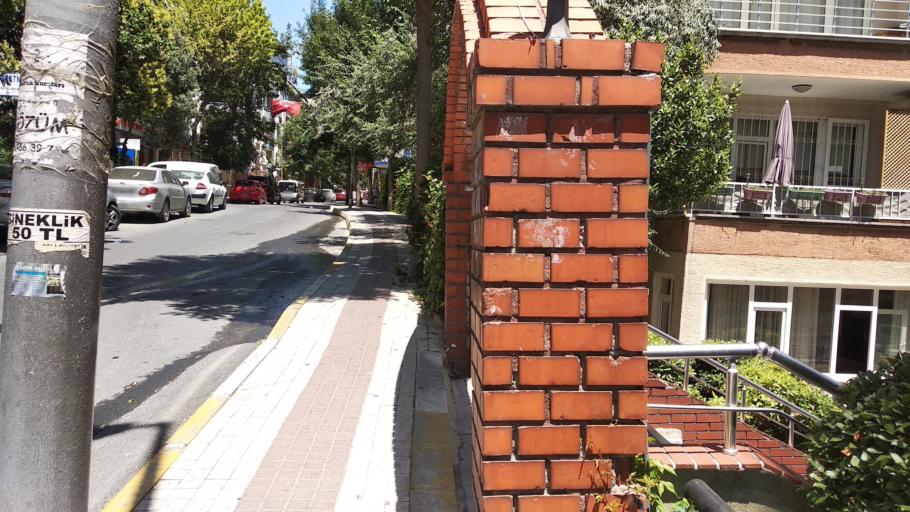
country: TR
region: Istanbul
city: Yakuplu
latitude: 40.9745
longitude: 28.7200
